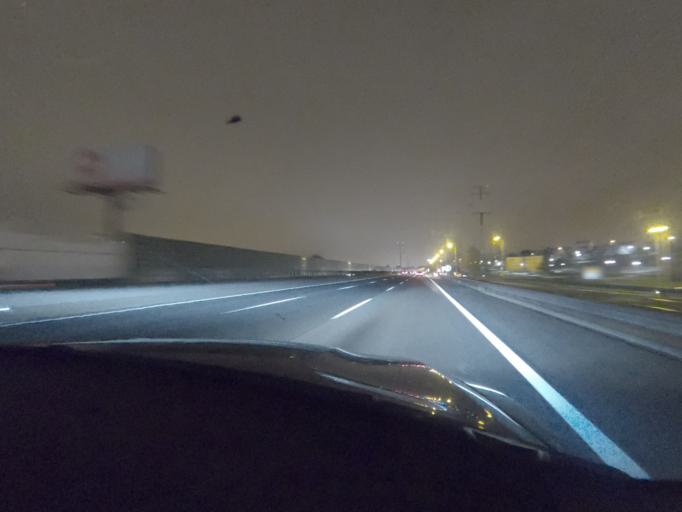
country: PT
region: Lisbon
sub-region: Loures
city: Sao Joao da Talha
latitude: 38.8233
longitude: -9.0994
